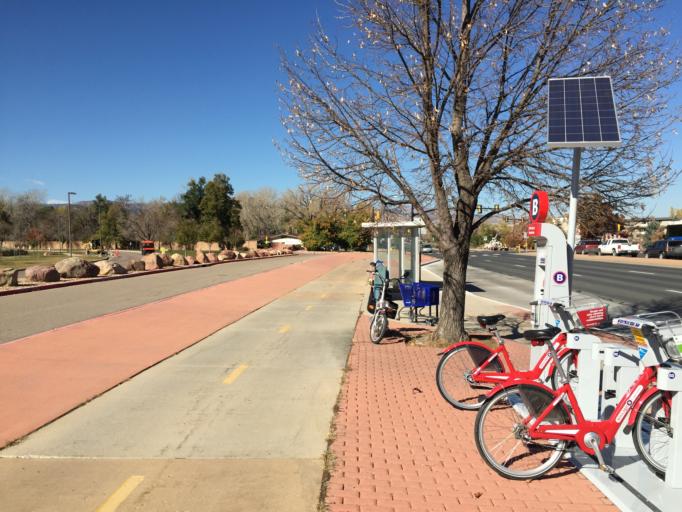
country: US
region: Colorado
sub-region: Boulder County
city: Boulder
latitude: 39.9957
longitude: -105.2608
